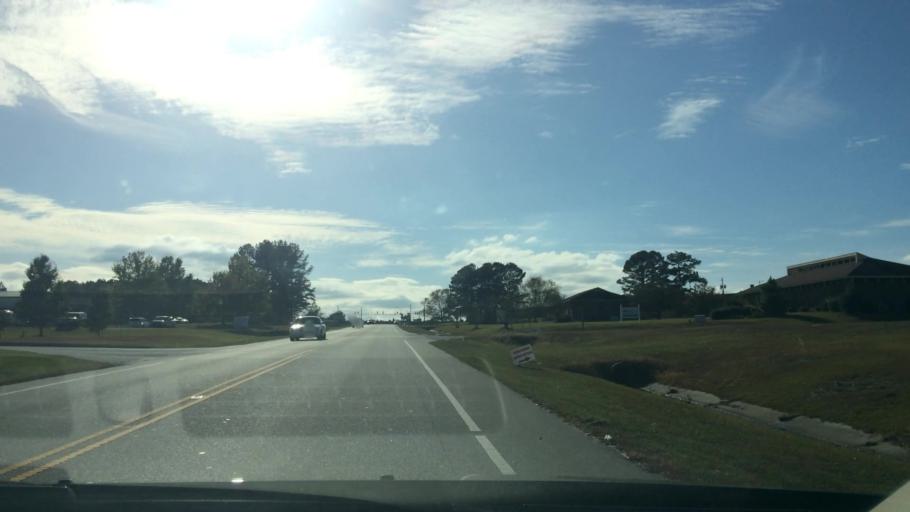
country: US
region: North Carolina
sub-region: Greene County
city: Snow Hill
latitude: 35.4546
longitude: -77.6821
